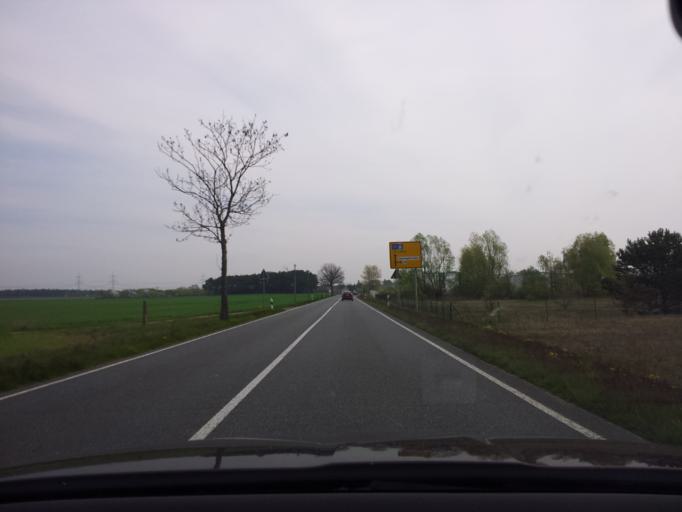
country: DE
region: Brandenburg
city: Luckau
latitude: 51.8916
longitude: 13.7944
